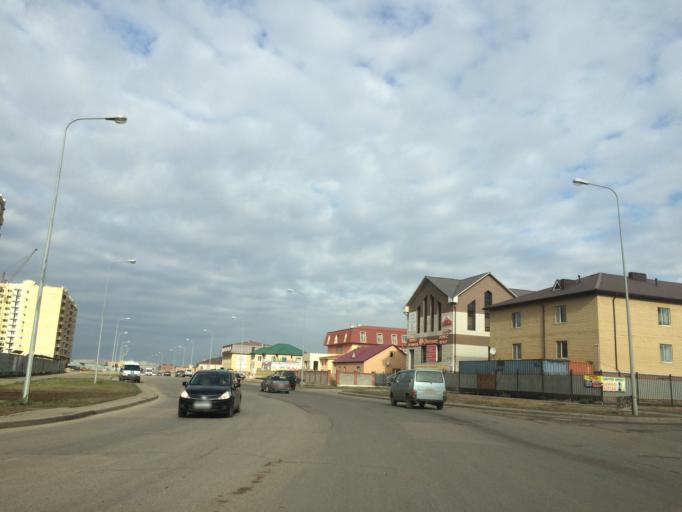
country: KZ
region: Astana Qalasy
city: Astana
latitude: 51.1722
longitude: 71.3725
